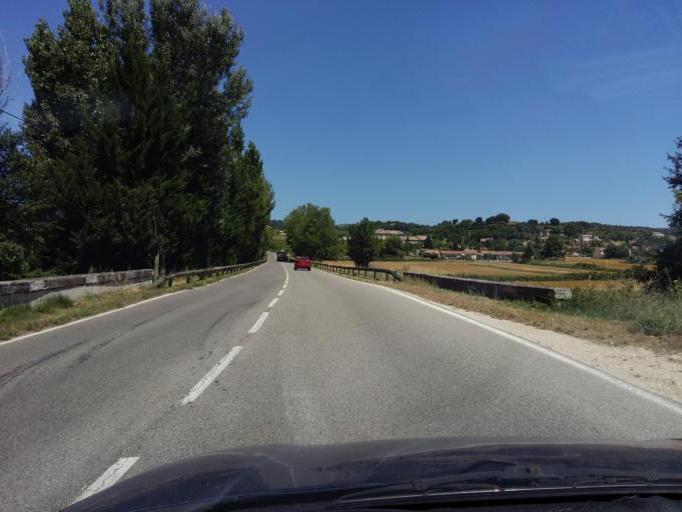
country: FR
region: Provence-Alpes-Cote d'Azur
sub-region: Departement du Vaucluse
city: Visan
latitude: 44.3086
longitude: 4.9482
